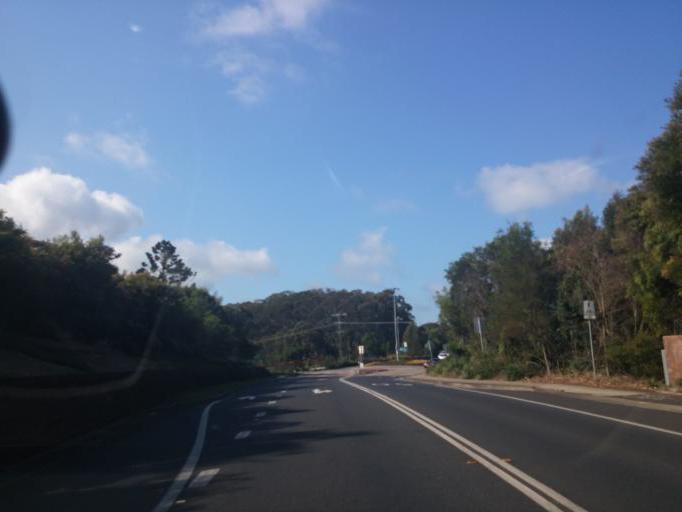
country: AU
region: New South Wales
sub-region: Coffs Harbour
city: Coffs Harbour
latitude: -30.2934
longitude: 153.1323
